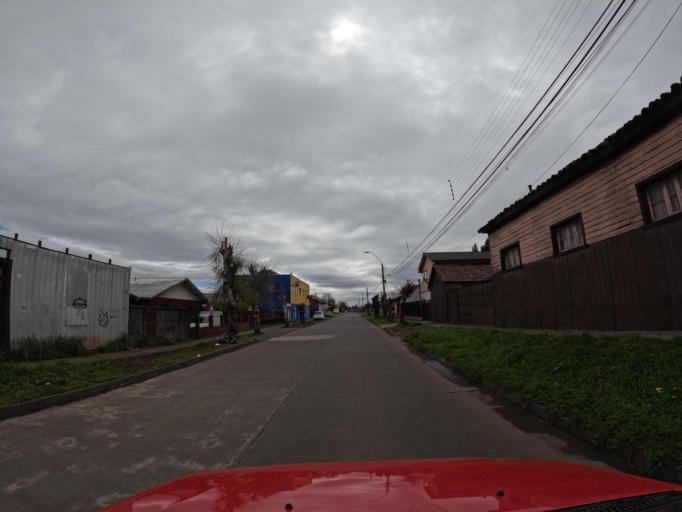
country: CL
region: Araucania
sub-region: Provincia de Malleco
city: Victoria
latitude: -38.2322
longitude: -72.3282
